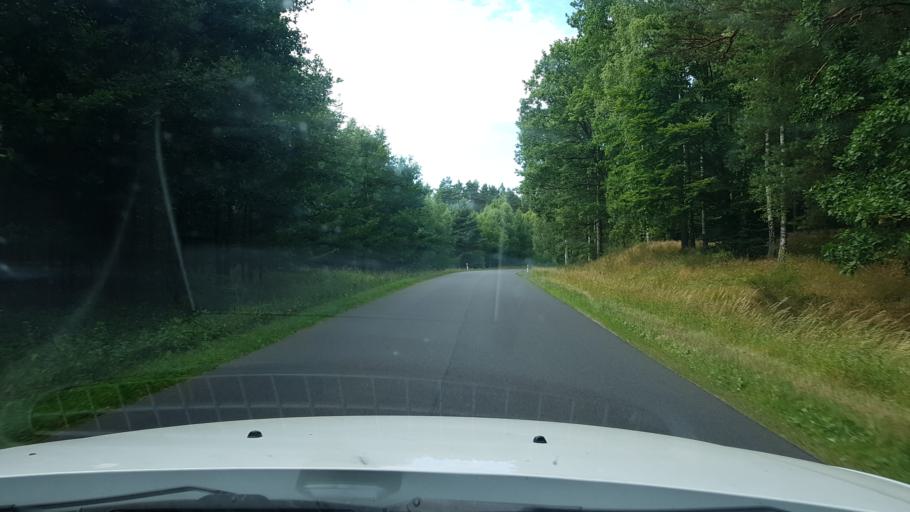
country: PL
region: West Pomeranian Voivodeship
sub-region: Powiat drawski
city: Zlocieniec
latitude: 53.5111
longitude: 16.0239
